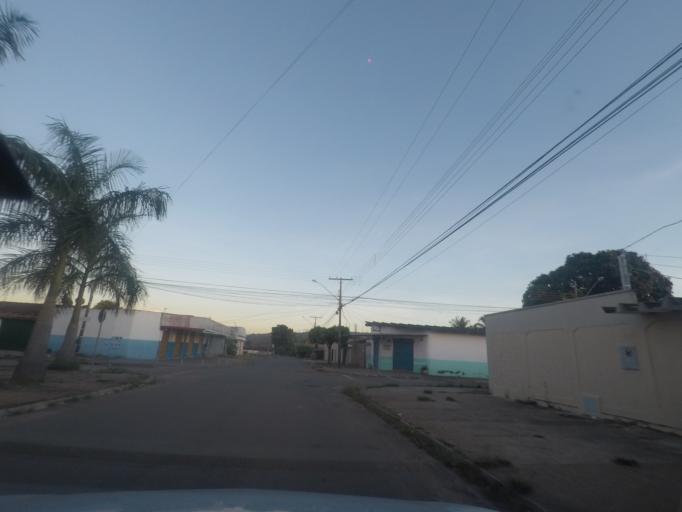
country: BR
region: Goias
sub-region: Goiania
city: Goiania
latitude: -16.6904
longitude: -49.3355
